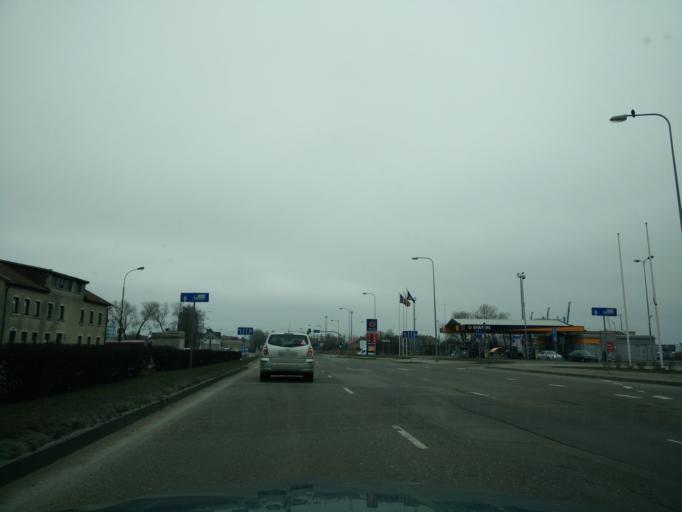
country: LT
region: Klaipedos apskritis
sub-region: Klaipeda
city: Klaipeda
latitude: 55.6886
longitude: 21.1451
